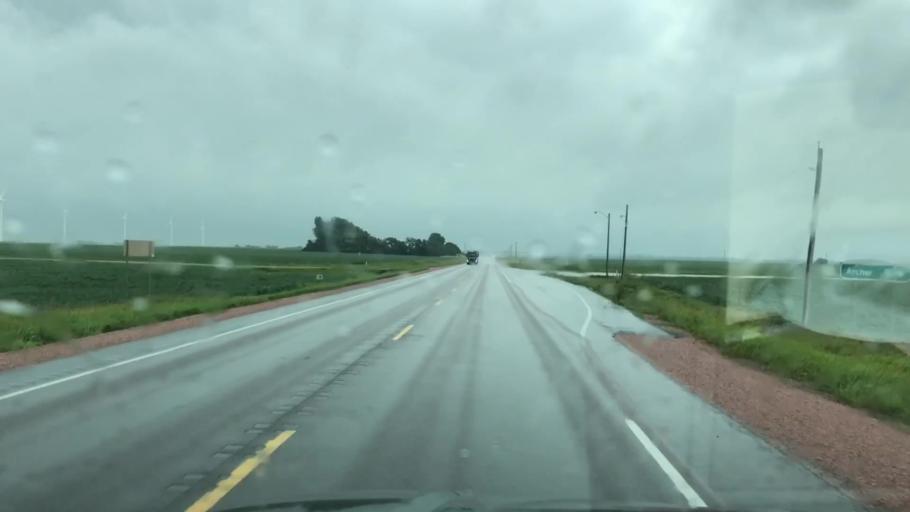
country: US
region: Iowa
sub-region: O'Brien County
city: Sanborn
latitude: 43.1862
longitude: -95.7554
